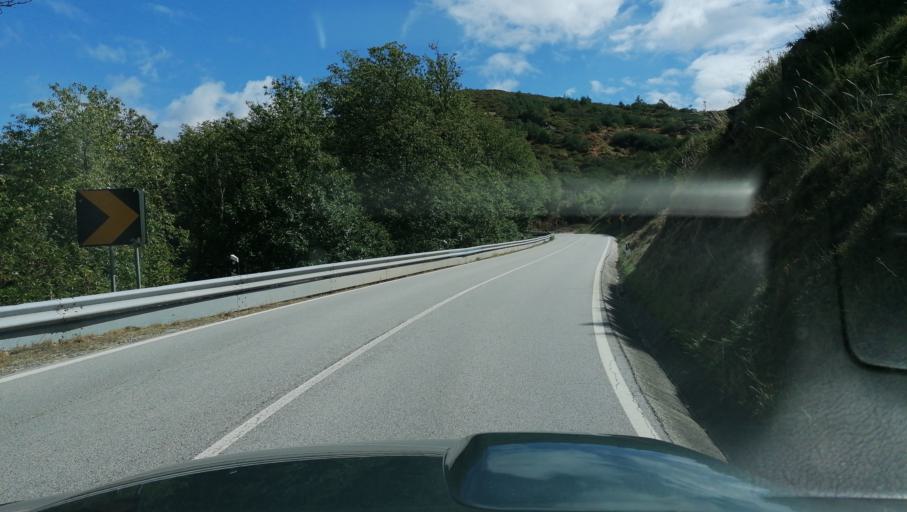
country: PT
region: Vila Real
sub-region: Vila Pouca de Aguiar
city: Vila Pouca de Aguiar
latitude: 41.5102
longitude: -7.6167
